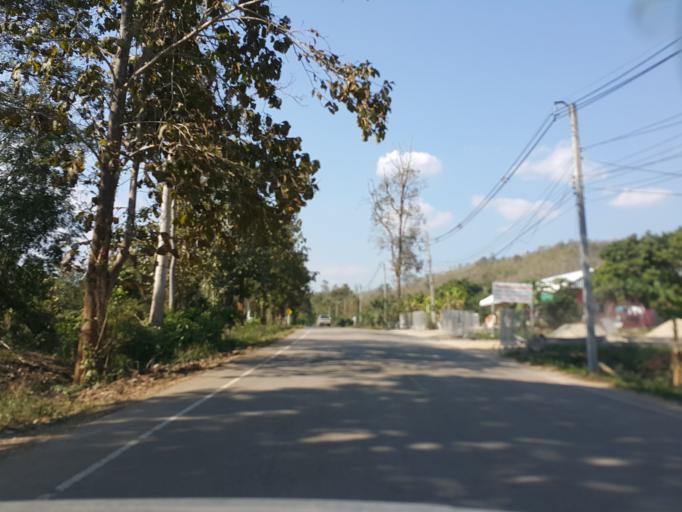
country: TH
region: Chiang Mai
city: Mae Wang
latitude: 18.6424
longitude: 98.6996
